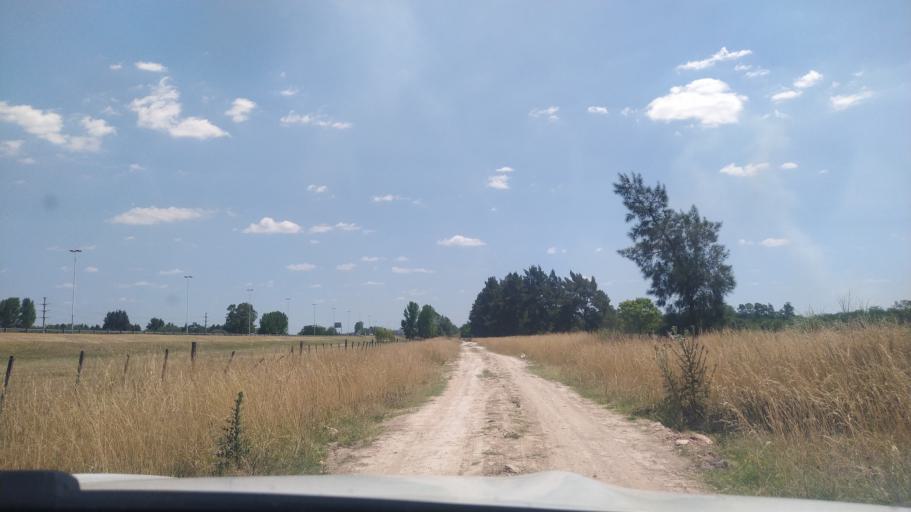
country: AR
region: Buenos Aires
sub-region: Partido de Ezeiza
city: Ezeiza
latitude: -34.9107
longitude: -58.6287
